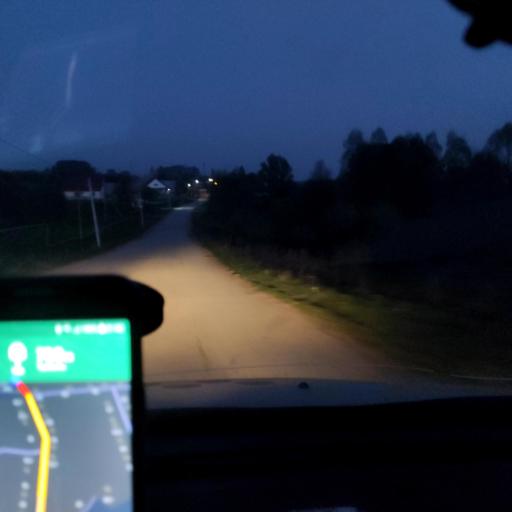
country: RU
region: Bashkortostan
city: Kabakovo
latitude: 54.6563
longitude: 56.3011
